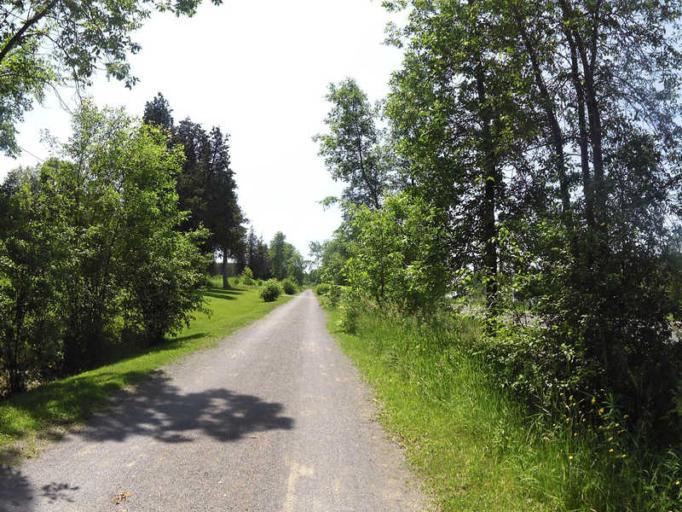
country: CA
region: Ontario
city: Peterborough
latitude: 44.4122
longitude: -78.2623
